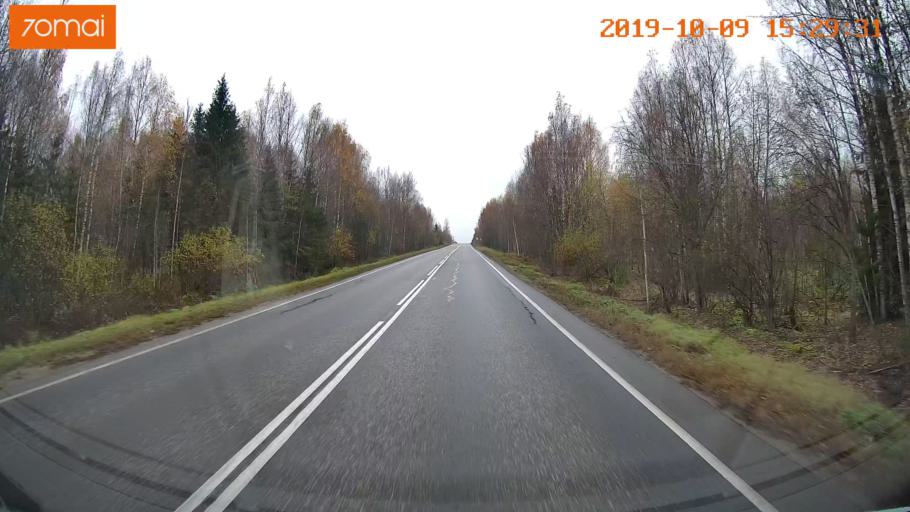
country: RU
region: Kostroma
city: Susanino
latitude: 57.9905
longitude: 41.3414
